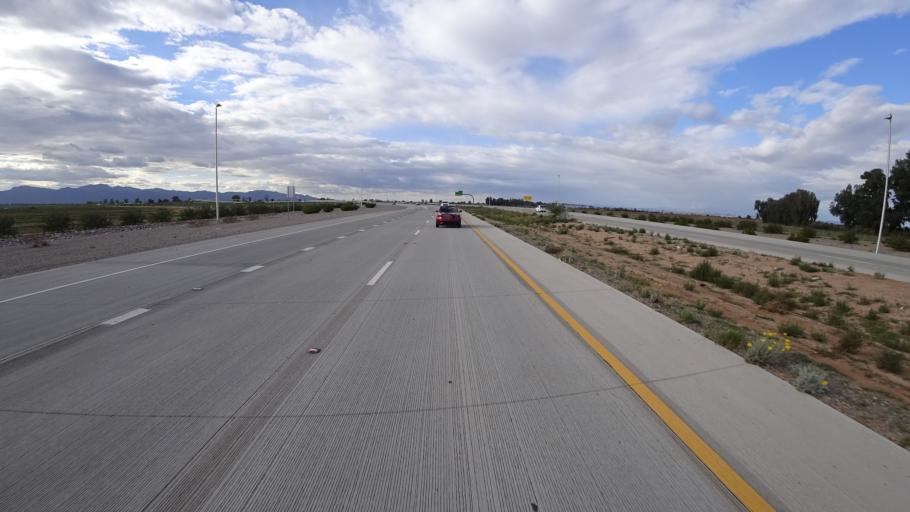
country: US
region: Arizona
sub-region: Maricopa County
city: Litchfield Park
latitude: 33.5546
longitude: -112.3531
